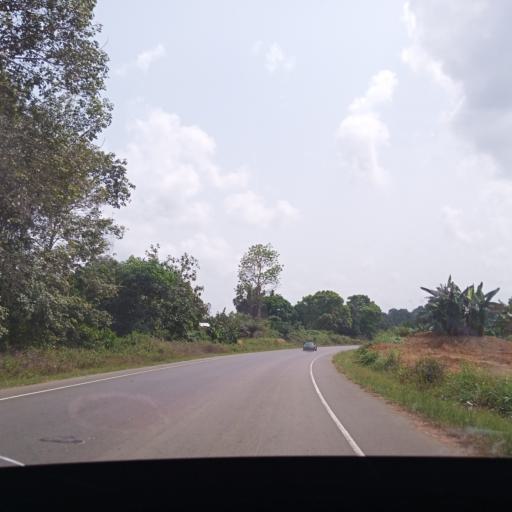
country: LR
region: Margibi
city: Kakata
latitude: 6.2500
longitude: -10.2961
